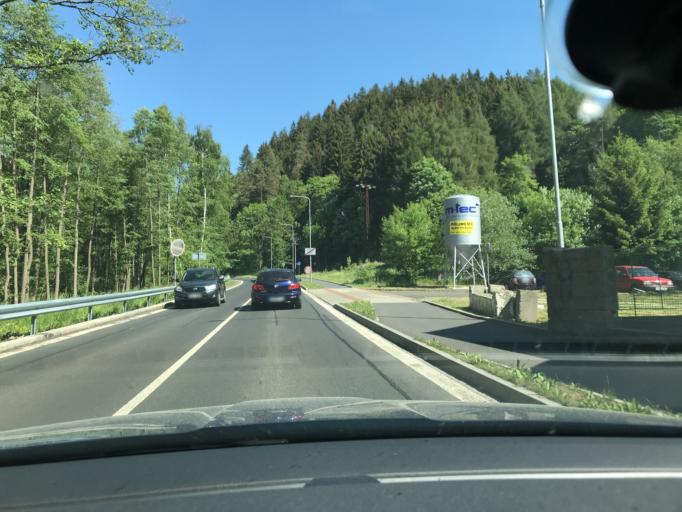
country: CZ
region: Karlovarsky
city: Jachymov
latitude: 50.3384
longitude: 12.9392
